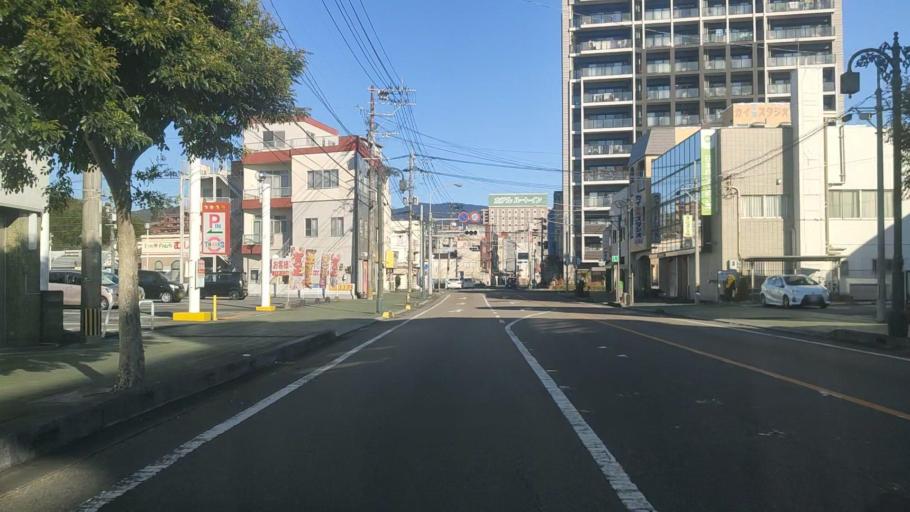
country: JP
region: Miyazaki
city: Nobeoka
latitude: 32.5859
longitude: 131.6712
